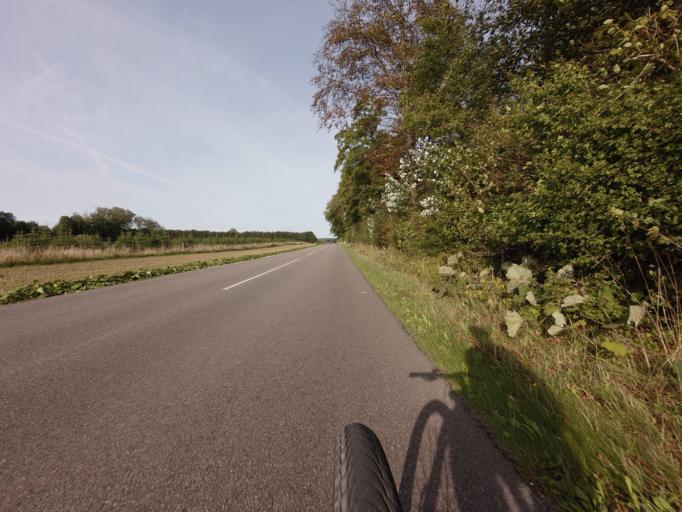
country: DK
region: Zealand
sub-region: Faxe Kommune
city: Fakse
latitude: 55.1991
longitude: 12.1247
